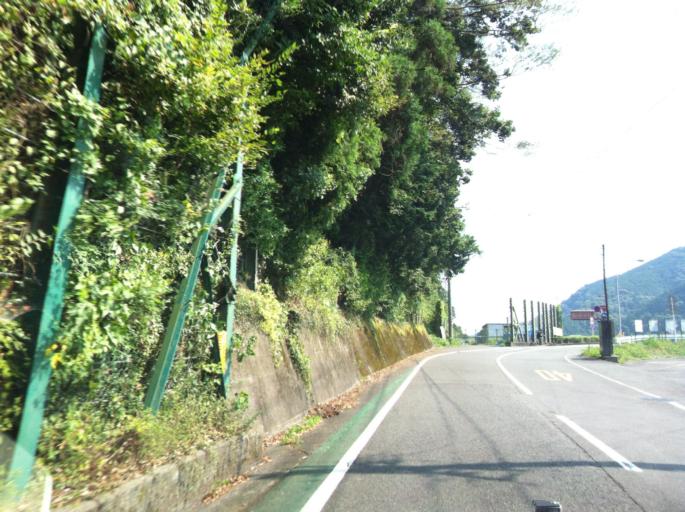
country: JP
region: Shizuoka
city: Shizuoka-shi
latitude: 35.1068
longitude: 138.3662
